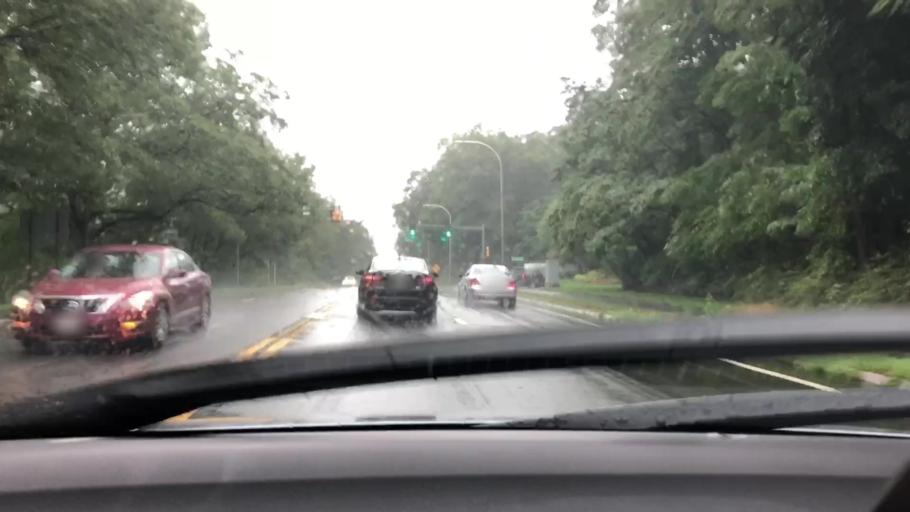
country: US
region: Massachusetts
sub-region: Norfolk County
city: Norwood
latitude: 42.2117
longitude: -71.1921
